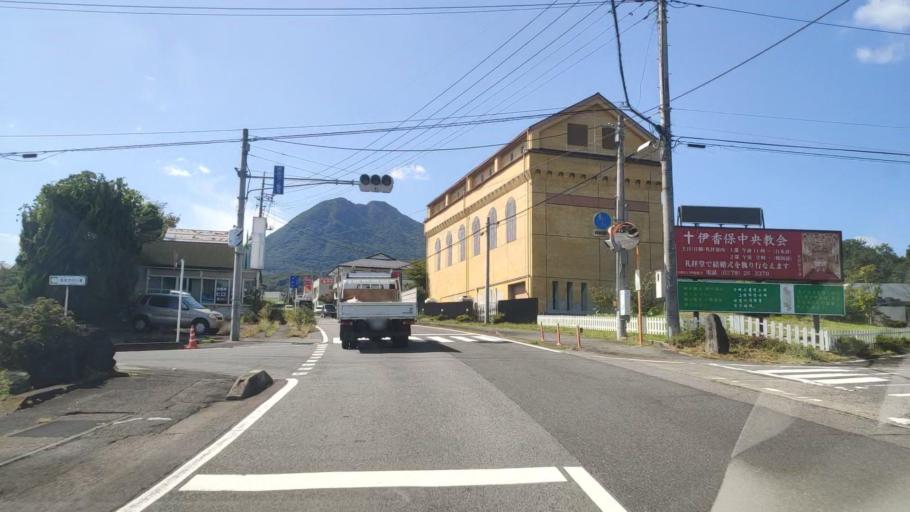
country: JP
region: Gunma
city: Shibukawa
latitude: 36.5003
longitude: 138.9595
